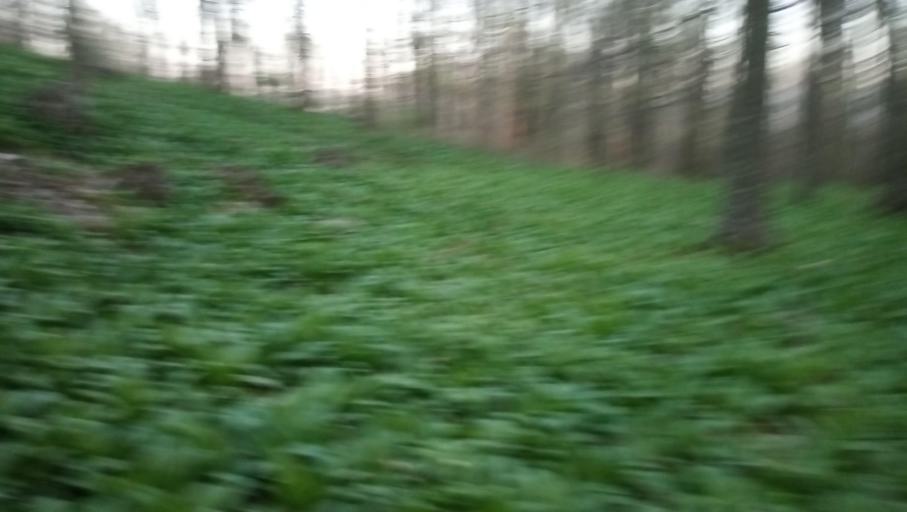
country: HU
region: Veszprem
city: Herend
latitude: 47.1890
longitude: 17.7473
